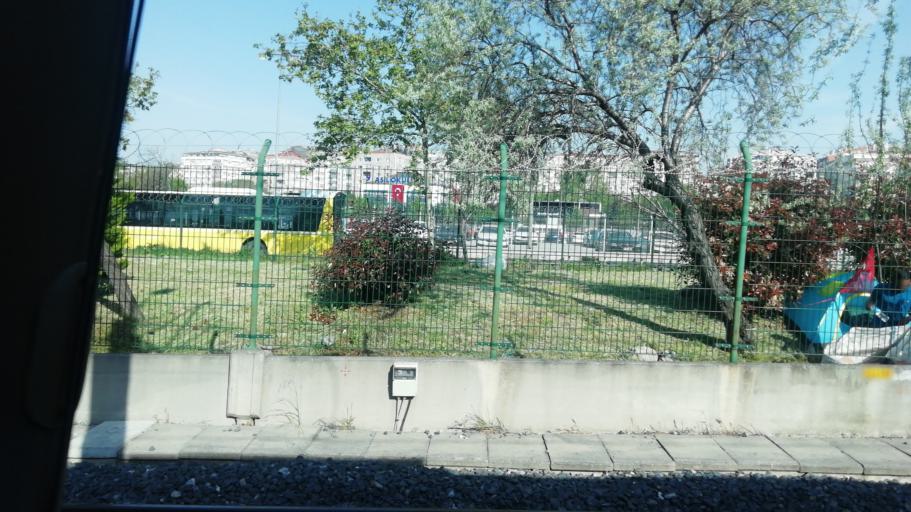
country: TR
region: Istanbul
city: guengoeren merter
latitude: 41.0031
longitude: 28.8932
